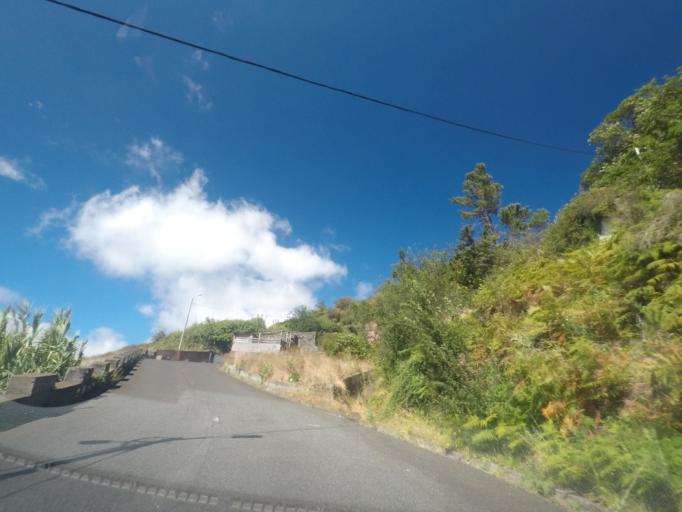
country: PT
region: Madeira
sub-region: Ribeira Brava
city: Campanario
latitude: 32.6927
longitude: -17.0371
